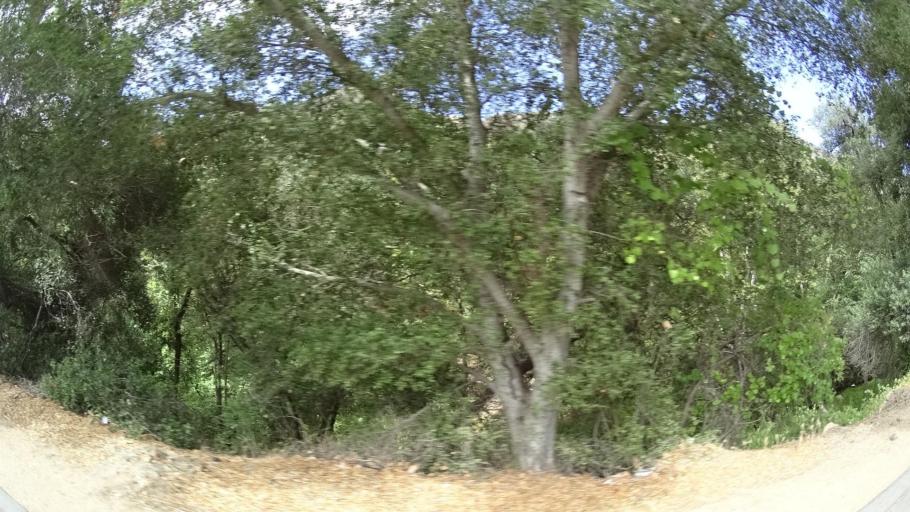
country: US
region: California
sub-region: San Diego County
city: Fallbrook
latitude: 33.4160
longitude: -117.2466
